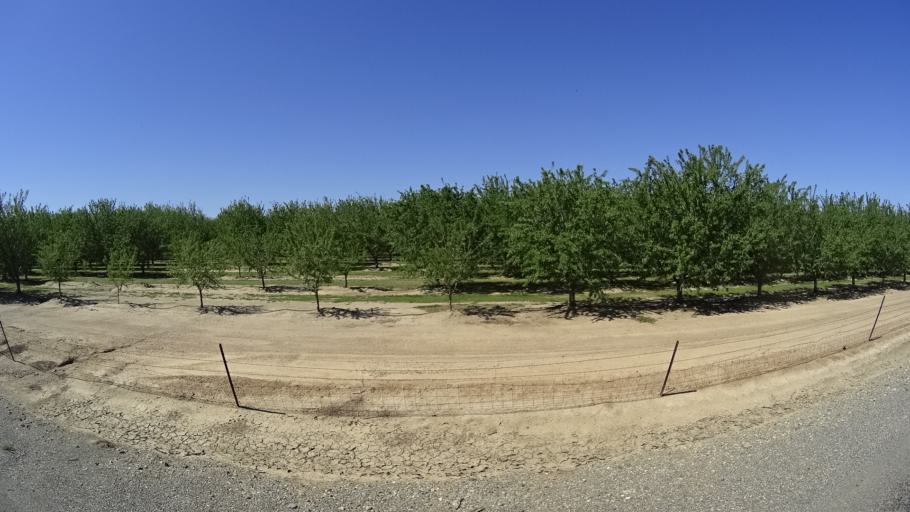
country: US
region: California
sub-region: Glenn County
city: Orland
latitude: 39.6496
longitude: -122.2346
